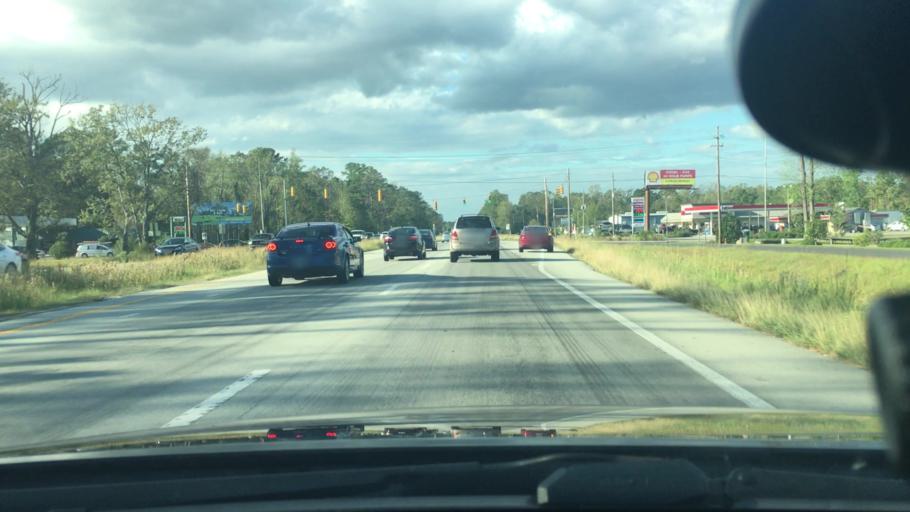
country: US
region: North Carolina
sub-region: Craven County
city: Fairfield Harbour
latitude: 35.0370
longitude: -77.0066
